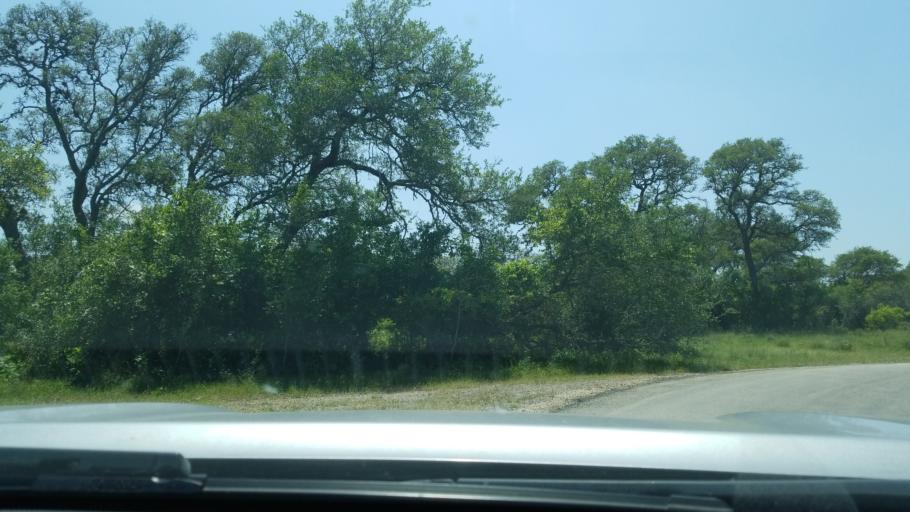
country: US
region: Texas
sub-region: Blanco County
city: Blanco
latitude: 30.0125
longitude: -98.4389
